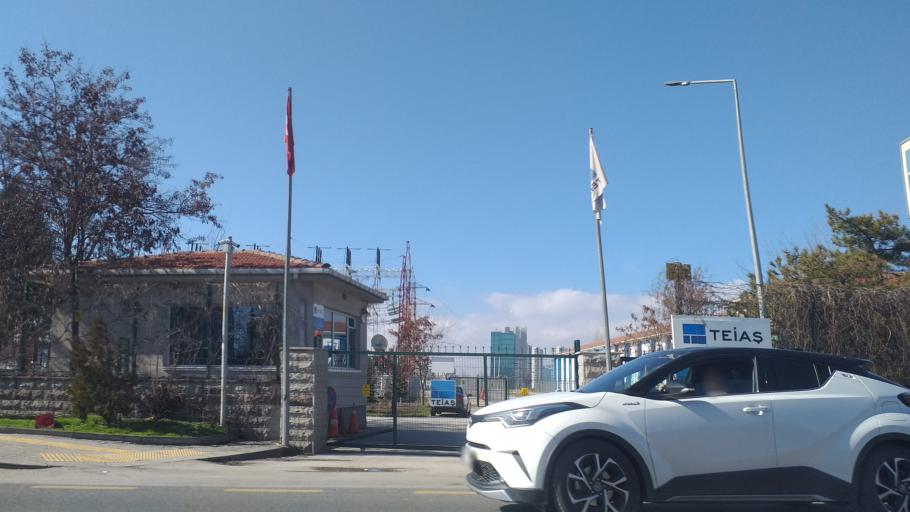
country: TR
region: Ankara
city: Ankara
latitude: 39.9152
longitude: 32.8141
